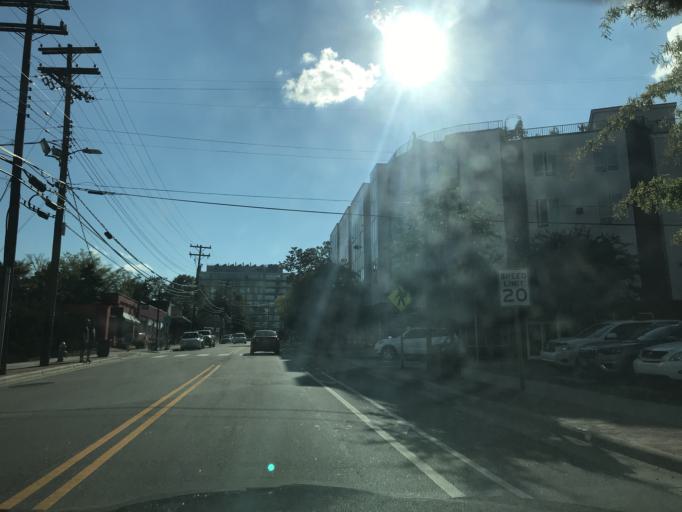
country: US
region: North Carolina
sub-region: Orange County
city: Chapel Hill
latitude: 35.9119
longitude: -79.0621
